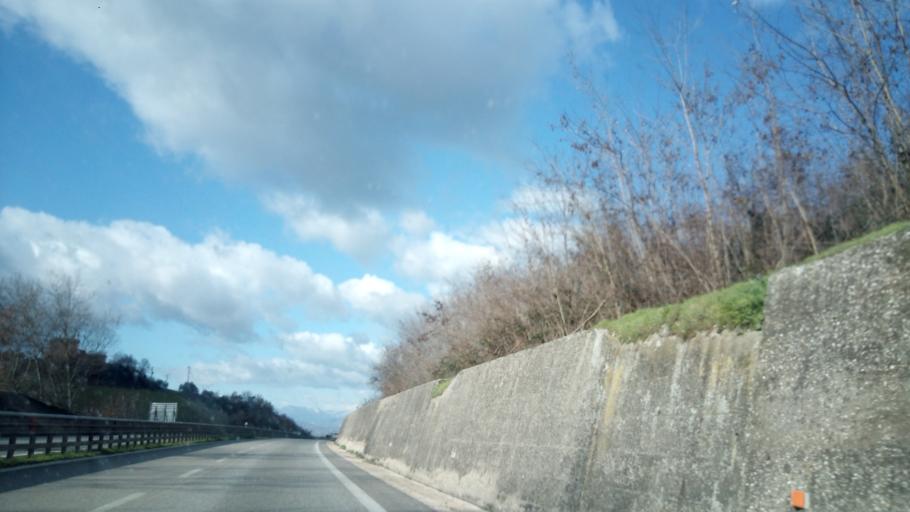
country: IT
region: Campania
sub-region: Provincia di Benevento
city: San Giorgio del Sannio
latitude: 41.0827
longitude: 14.8490
